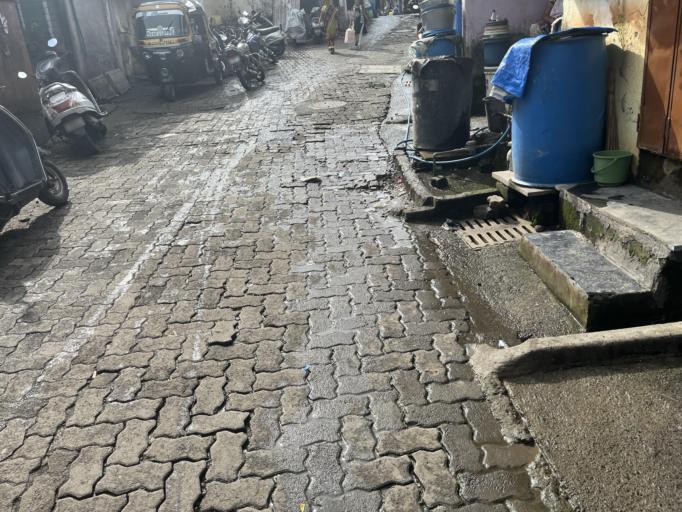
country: IN
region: Maharashtra
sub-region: Mumbai Suburban
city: Borivli
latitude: 19.2348
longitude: 72.8685
